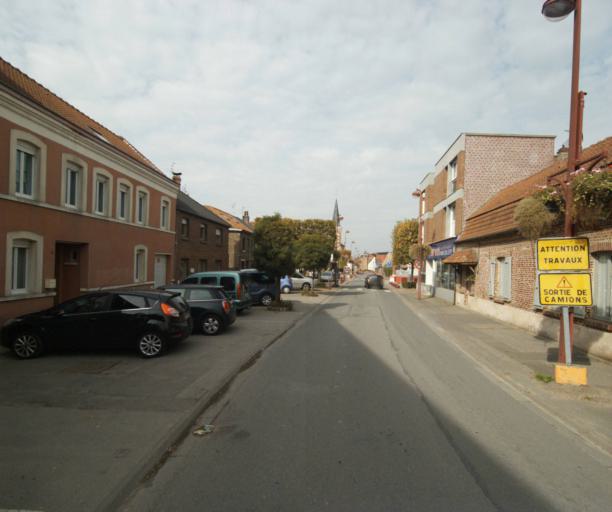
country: FR
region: Nord-Pas-de-Calais
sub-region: Departement du Nord
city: Templemars
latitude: 50.5703
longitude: 3.0546
